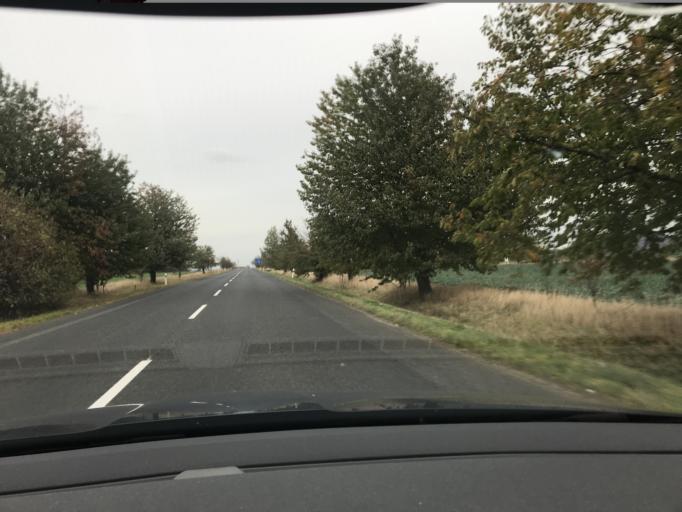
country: CZ
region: Ustecky
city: Roudnice nad Labem
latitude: 50.4150
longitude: 14.1943
